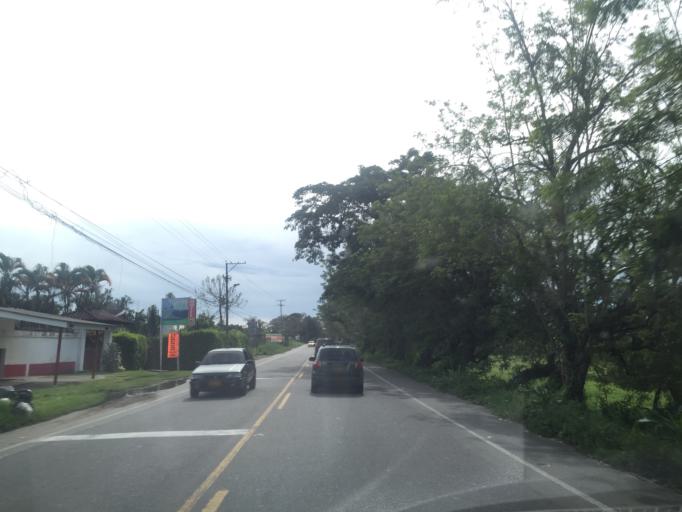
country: CO
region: Quindio
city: La Tebaida
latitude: 4.4784
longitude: -75.7530
